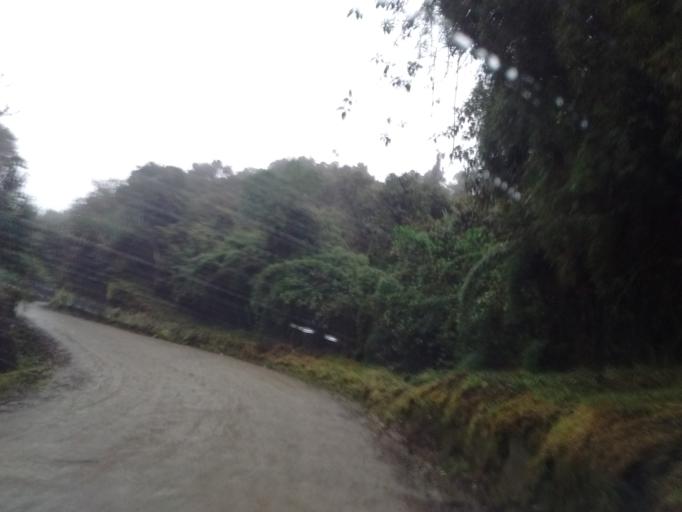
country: CO
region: Cauca
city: Paispamba
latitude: 2.1626
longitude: -76.4202
